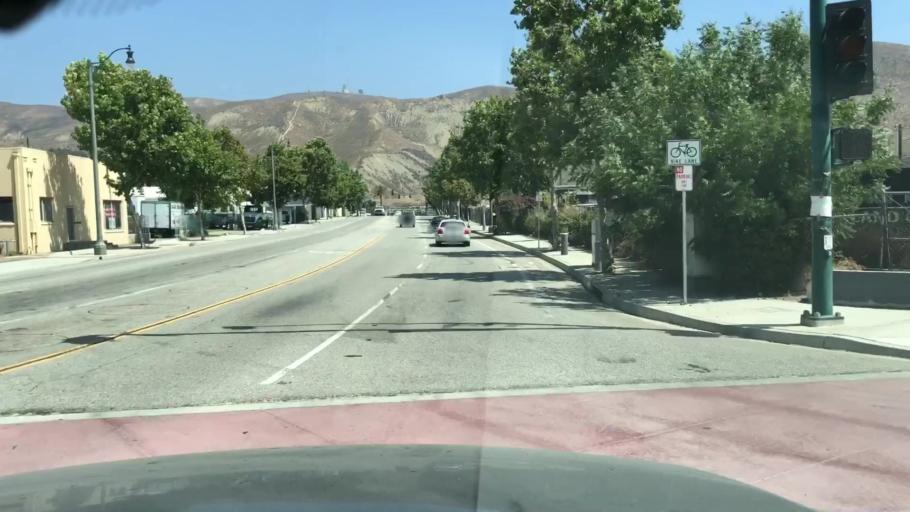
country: US
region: California
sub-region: Ventura County
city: Ventura
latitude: 34.3001
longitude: -119.2981
